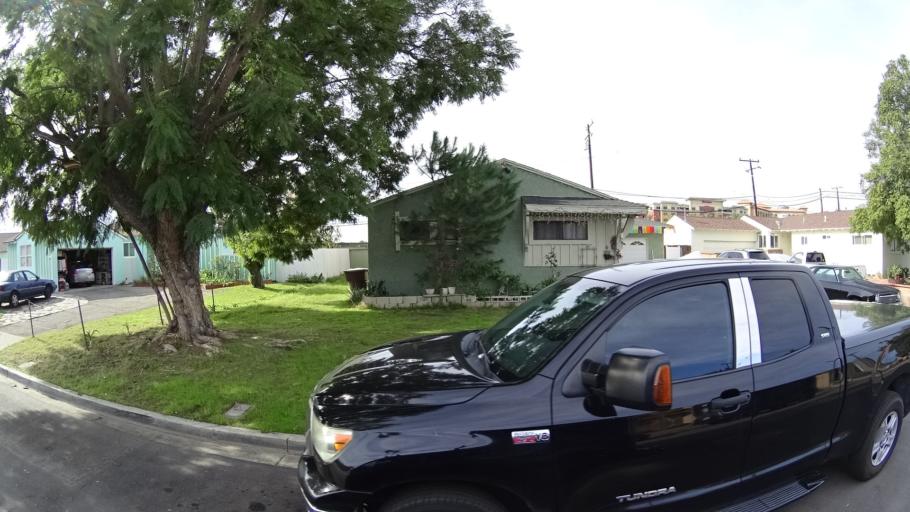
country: US
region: California
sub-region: Orange County
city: Garden Grove
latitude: 33.7850
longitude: -117.9132
